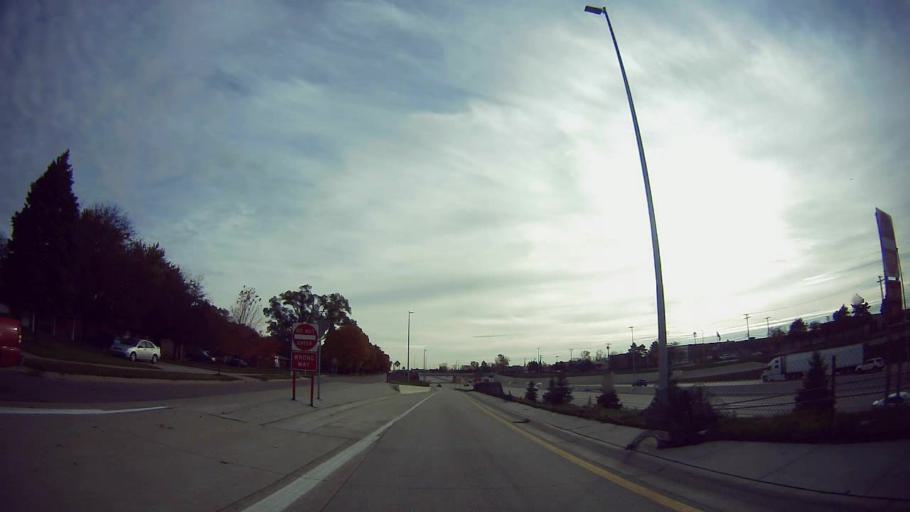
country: US
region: Michigan
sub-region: Wayne County
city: Livonia
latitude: 42.3835
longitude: -83.3515
